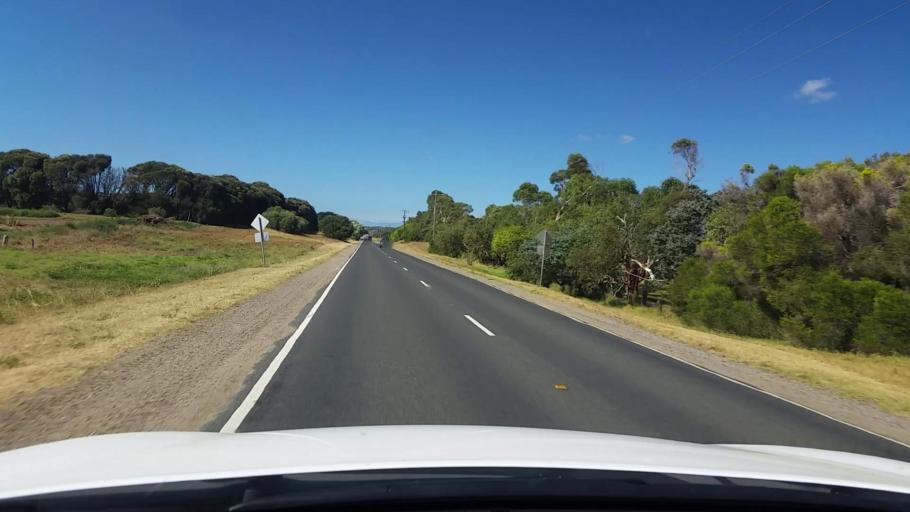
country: AU
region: Victoria
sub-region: Mornington Peninsula
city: Rosebud West
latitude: -38.3998
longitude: 144.8880
